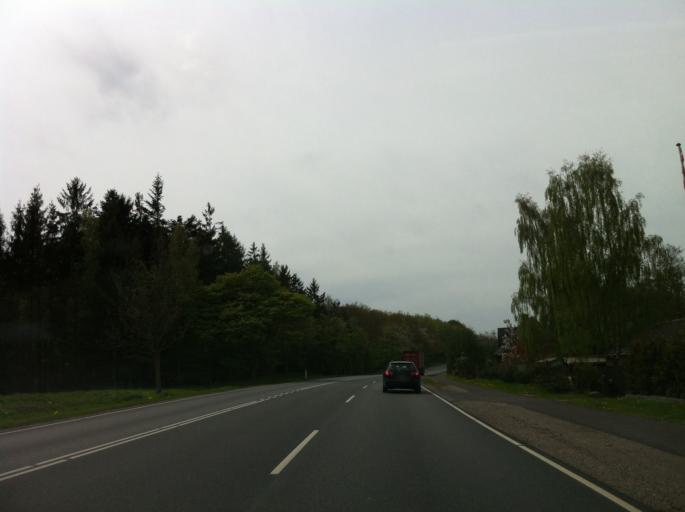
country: DK
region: Zealand
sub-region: Lejre Kommune
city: Osted
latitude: 55.5402
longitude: 11.9285
